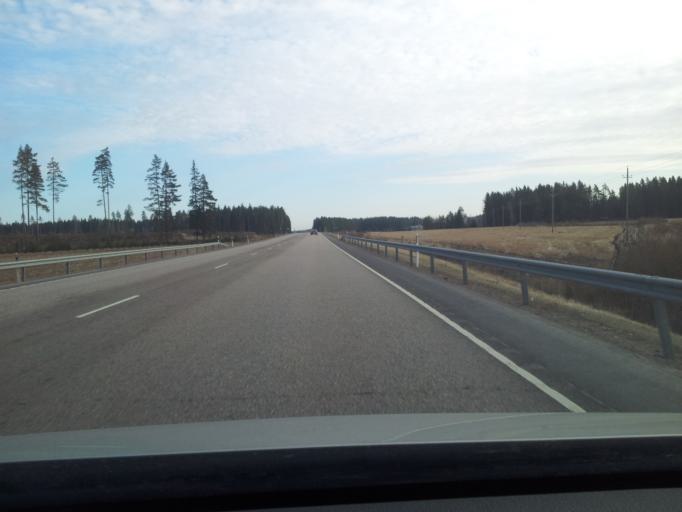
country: FI
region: Kymenlaakso
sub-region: Kouvola
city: Elimaeki
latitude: 60.7801
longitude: 26.4893
